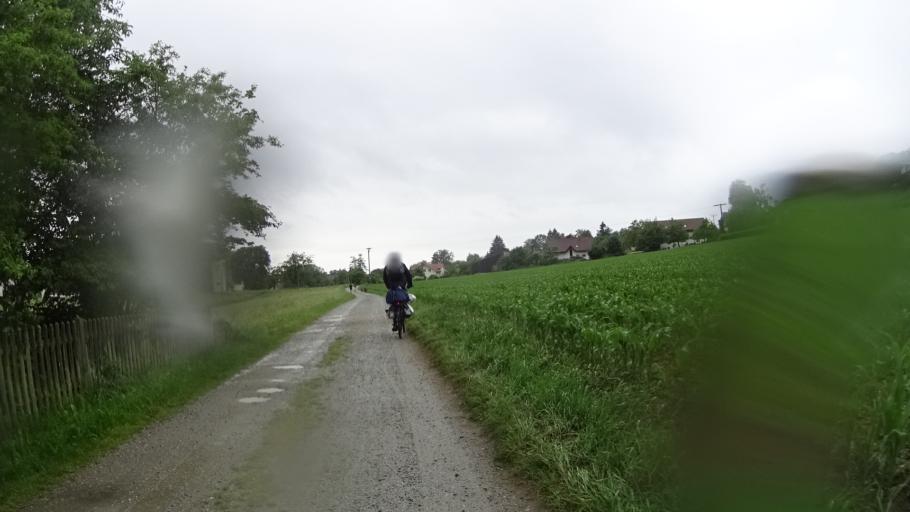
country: AT
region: Upper Austria
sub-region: Politischer Bezirk Scharding
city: Scharding
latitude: 48.4886
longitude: 13.4430
